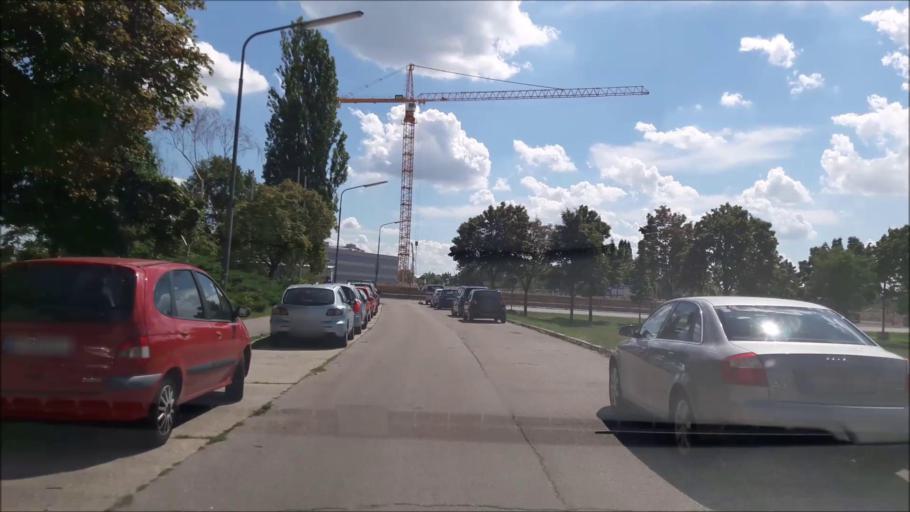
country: AT
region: Lower Austria
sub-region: Politischer Bezirk Wien-Umgebung
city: Gerasdorf bei Wien
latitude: 48.2338
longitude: 16.4690
